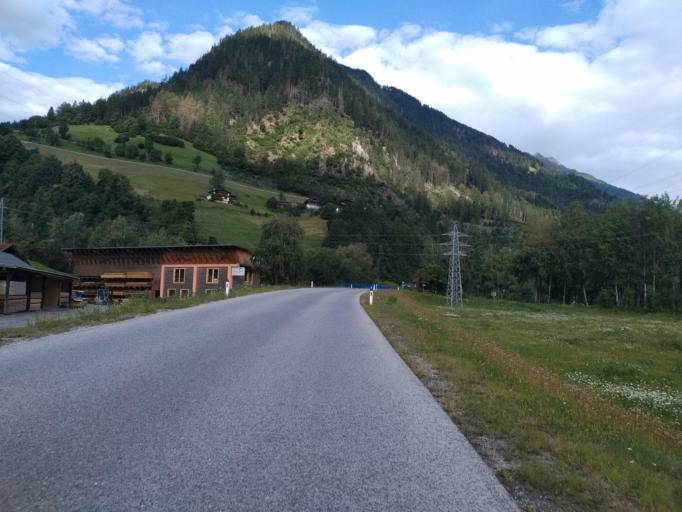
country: AT
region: Tyrol
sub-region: Politischer Bezirk Lienz
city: Hopfgarten in Defereggen
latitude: 46.9284
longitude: 12.5801
